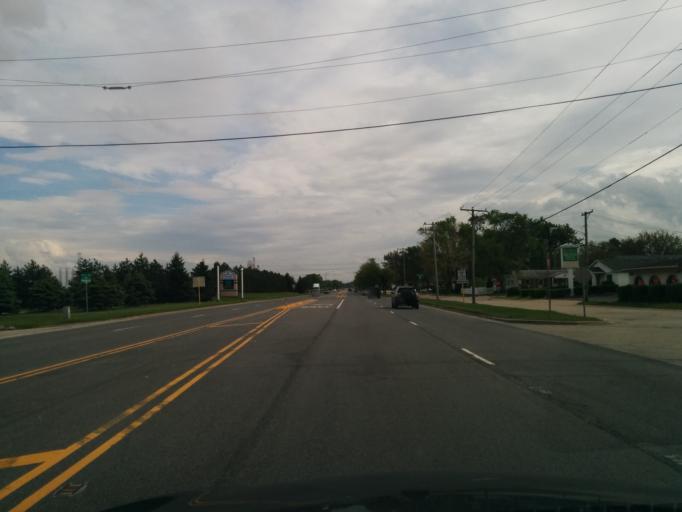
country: US
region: Illinois
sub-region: Will County
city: Romeoville
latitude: 41.6390
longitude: -88.0805
